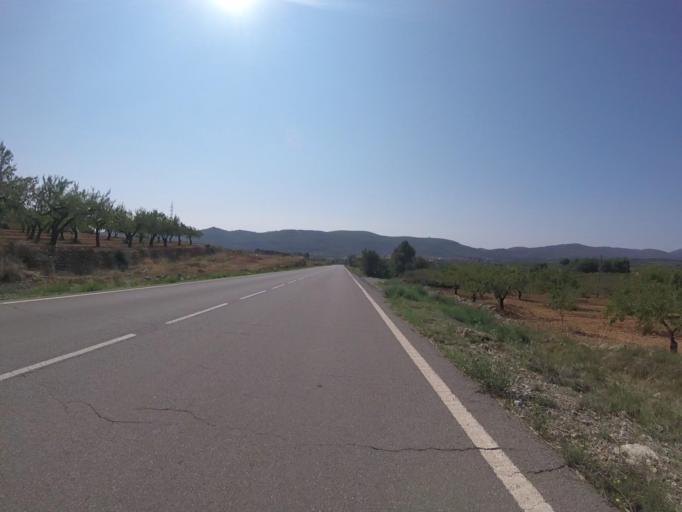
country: ES
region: Valencia
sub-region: Provincia de Castello
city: Adzaneta
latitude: 40.2296
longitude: -0.1757
